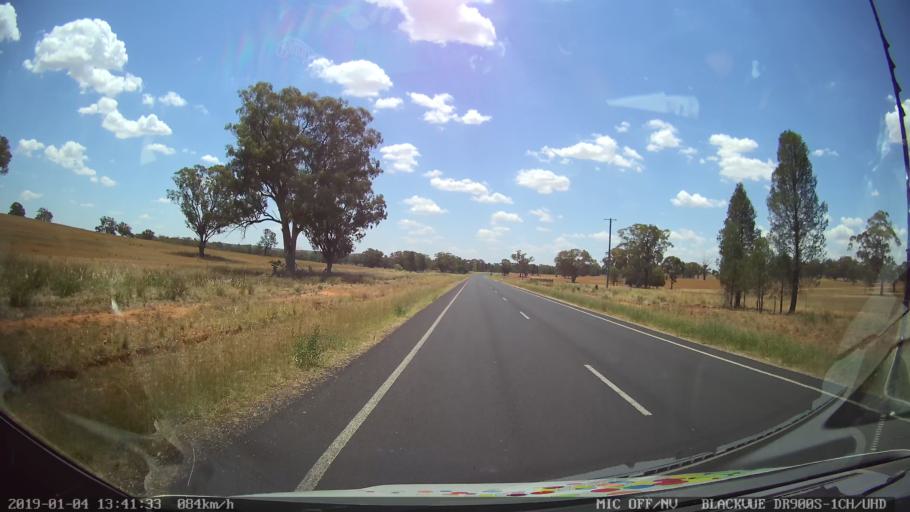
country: AU
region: New South Wales
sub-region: Dubbo Municipality
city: Dubbo
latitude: -32.5008
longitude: 148.5534
